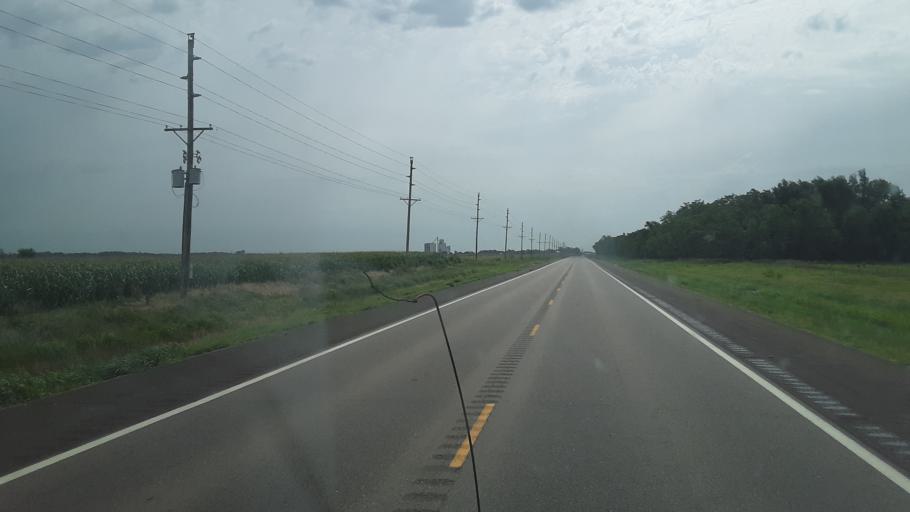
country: US
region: Kansas
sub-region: Stafford County
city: Stafford
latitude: 37.9549
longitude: -98.5192
